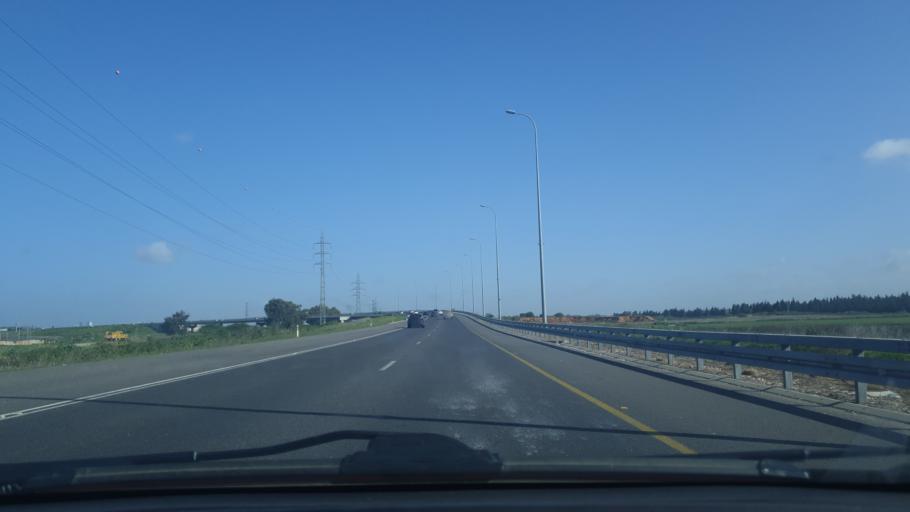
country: IL
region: Tel Aviv
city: Kefar Shemaryahu
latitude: 32.2090
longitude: 34.8371
